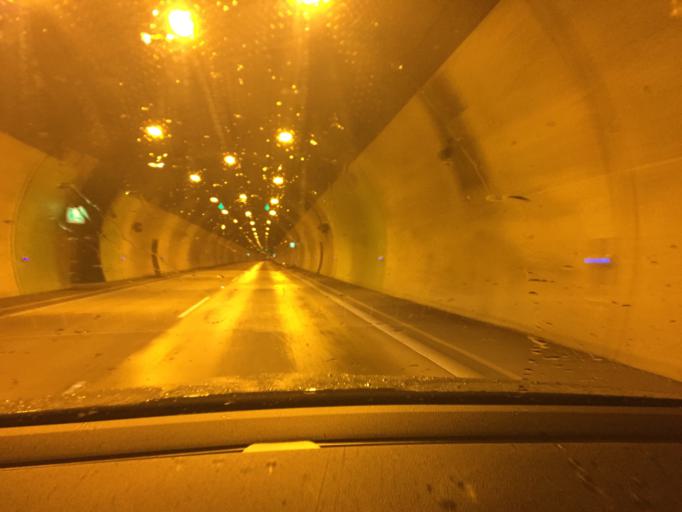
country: CZ
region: Ustecky
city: Libouchec
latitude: 50.7524
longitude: 13.9894
